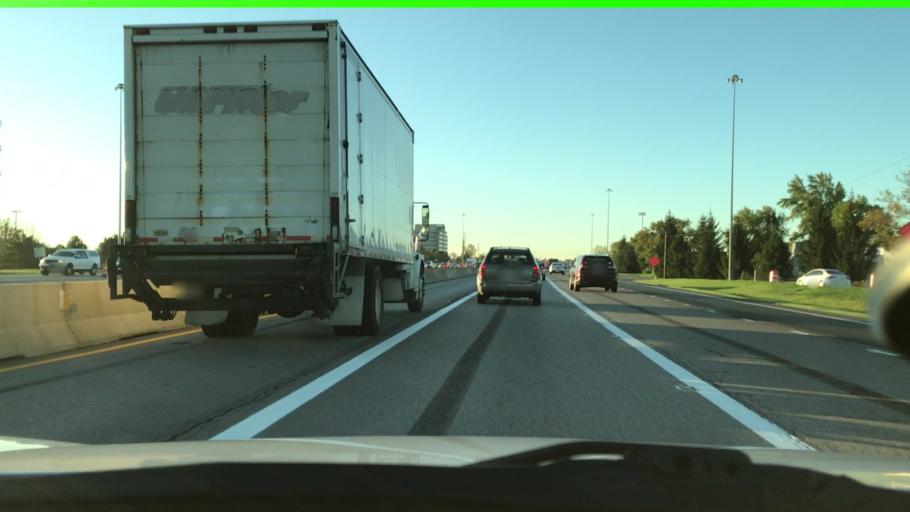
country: US
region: Ohio
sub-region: Franklin County
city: Hilliard
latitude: 40.0318
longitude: -83.1237
